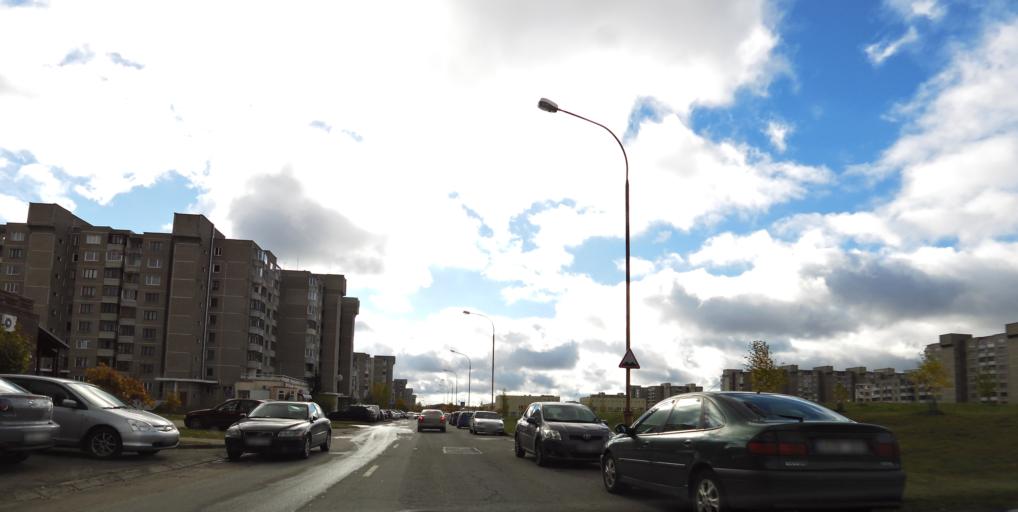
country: LT
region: Vilnius County
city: Pilaite
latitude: 54.7092
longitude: 25.1820
